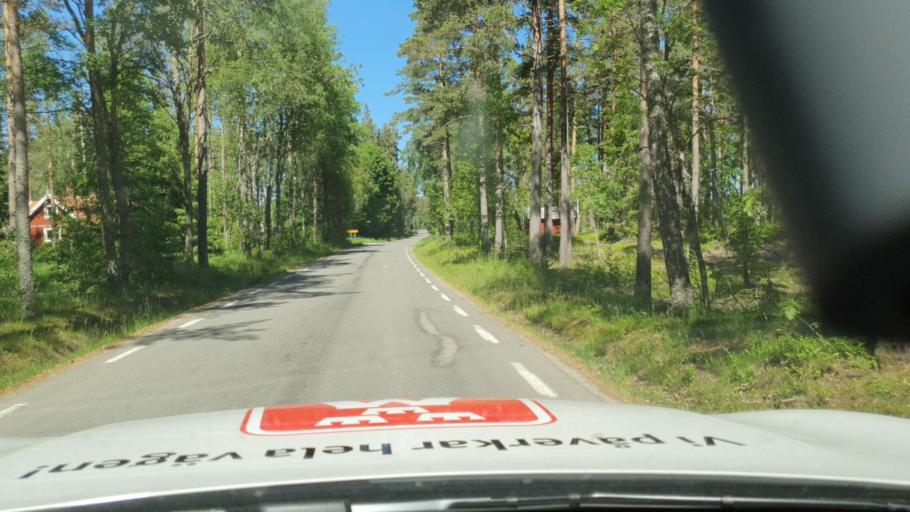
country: SE
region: Vaestra Goetaland
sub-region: Tidaholms Kommun
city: Tidaholm
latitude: 58.0876
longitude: 14.0721
